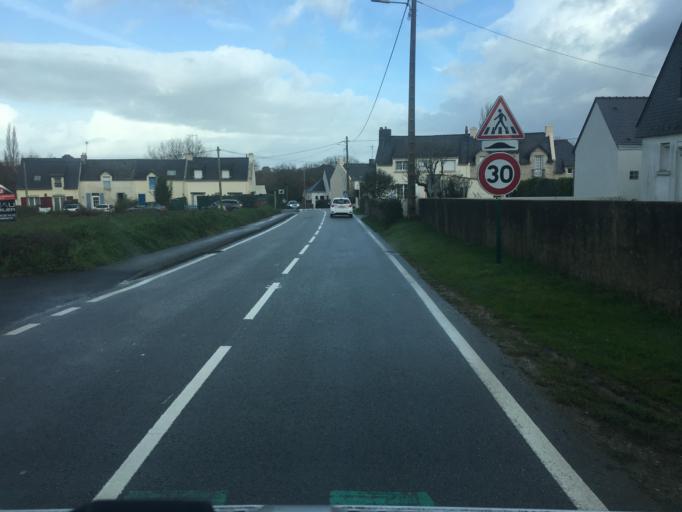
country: FR
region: Brittany
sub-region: Departement du Morbihan
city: Sarzeau
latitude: 47.5135
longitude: -2.7665
